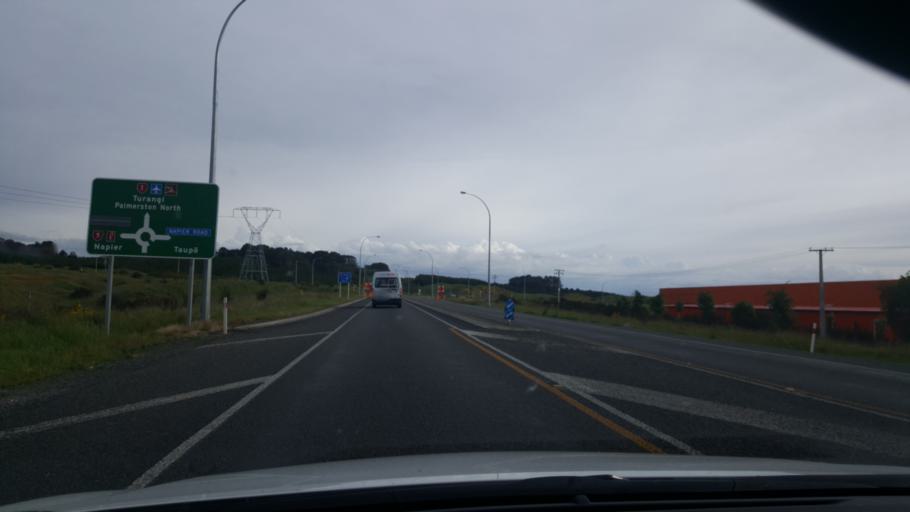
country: NZ
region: Waikato
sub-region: Taupo District
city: Taupo
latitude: -38.7020
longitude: 176.1118
